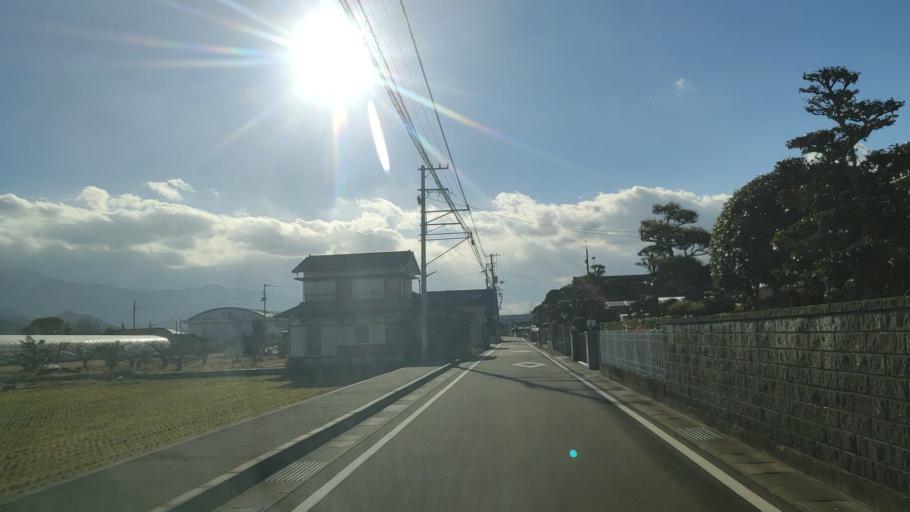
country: JP
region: Ehime
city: Saijo
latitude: 33.9147
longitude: 133.1025
